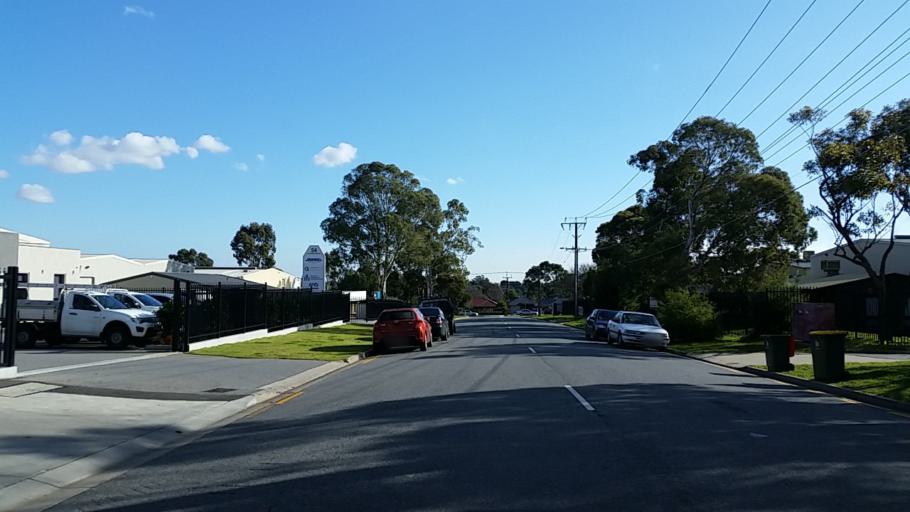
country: AU
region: South Australia
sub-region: Tea Tree Gully
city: Modbury
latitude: -34.8476
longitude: 138.6731
